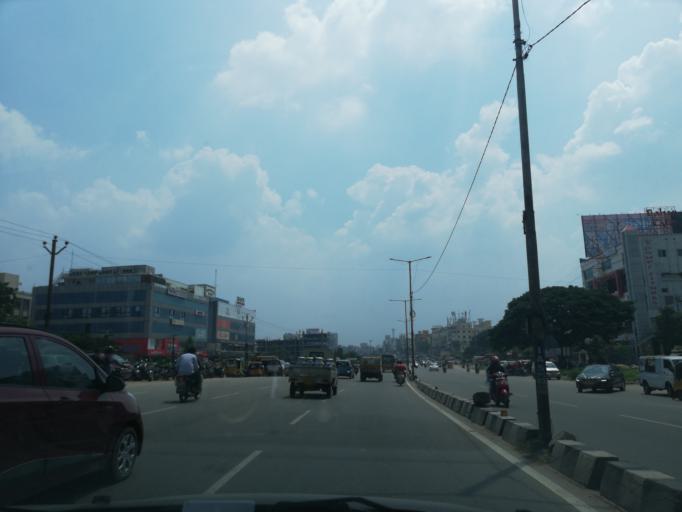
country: IN
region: Telangana
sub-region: Medak
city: Serilingampalle
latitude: 17.4955
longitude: 78.3372
